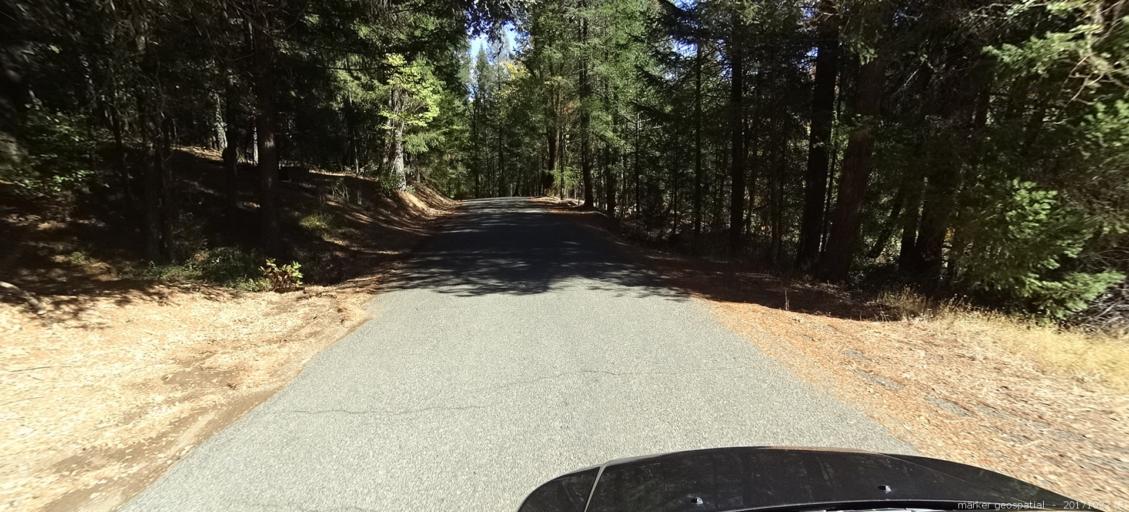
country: US
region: California
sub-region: Shasta County
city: Central Valley (historical)
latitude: 40.9329
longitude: -122.4627
